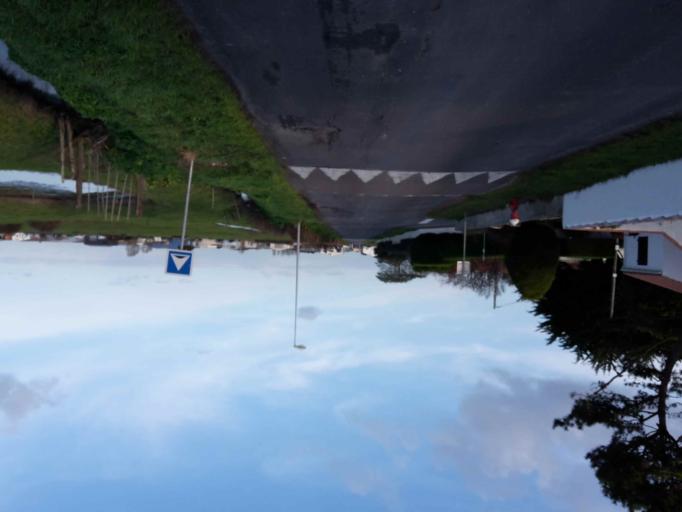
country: FR
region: Pays de la Loire
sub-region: Departement de la Vendee
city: La Gueriniere
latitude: 46.9689
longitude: -2.2481
